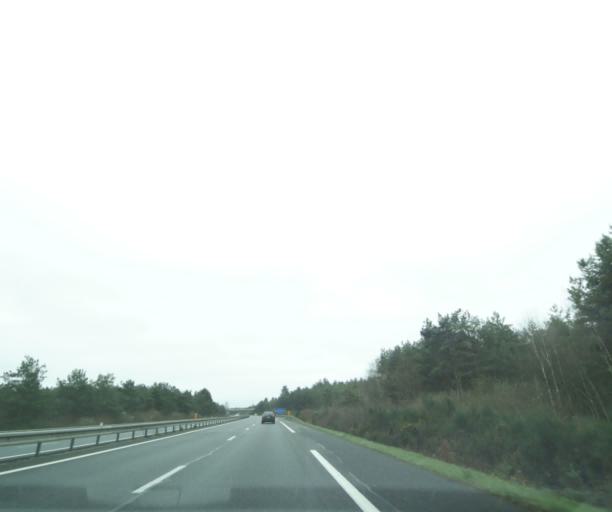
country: FR
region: Centre
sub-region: Departement du Loiret
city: La Ferte-Saint-Aubin
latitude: 47.6837
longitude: 1.9052
